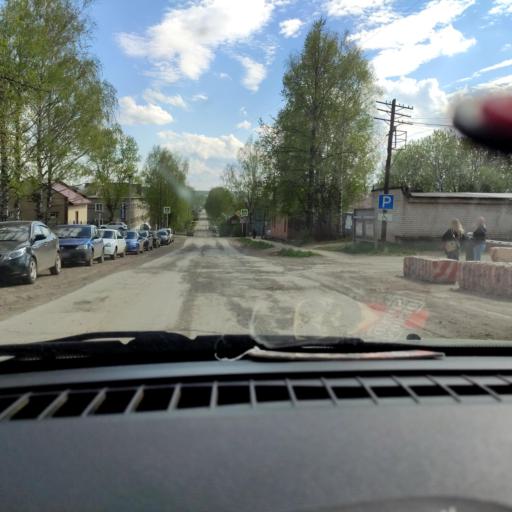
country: RU
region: Perm
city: Kudymkar
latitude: 59.0123
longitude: 54.6530
